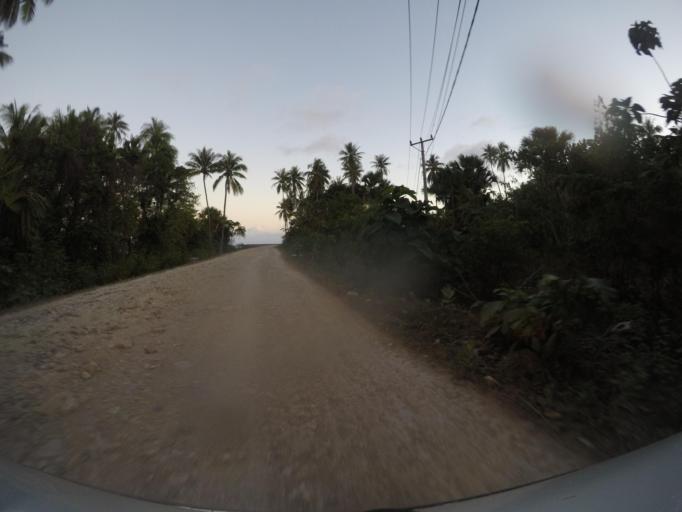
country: TL
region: Viqueque
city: Viqueque
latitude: -8.7836
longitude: 126.6356
